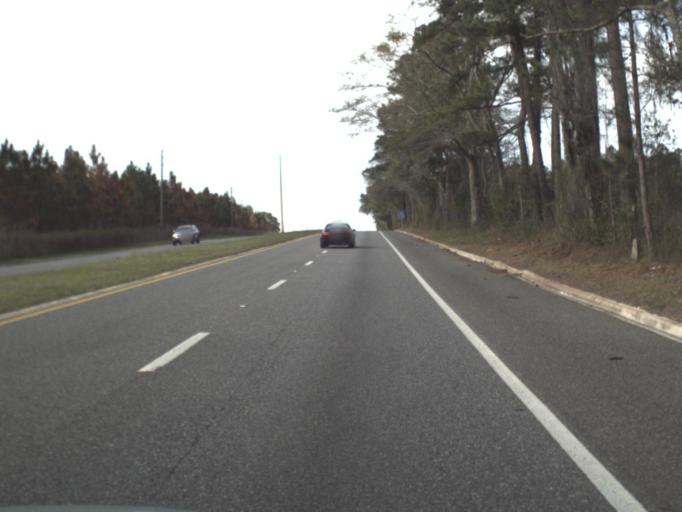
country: US
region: Florida
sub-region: Jefferson County
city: Monticello
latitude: 30.4134
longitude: -83.9111
